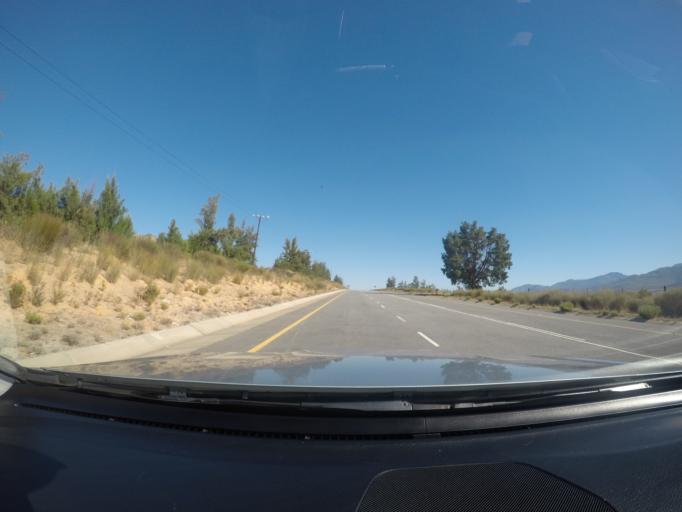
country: ZA
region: Western Cape
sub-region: West Coast District Municipality
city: Clanwilliam
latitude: -32.5430
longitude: 18.9784
